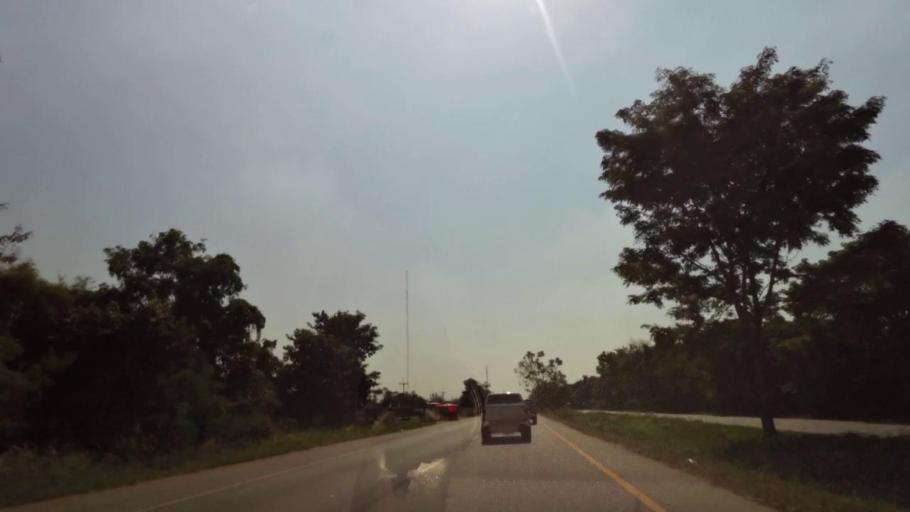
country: TH
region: Phichit
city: Wachira Barami
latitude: 16.4189
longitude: 100.1439
